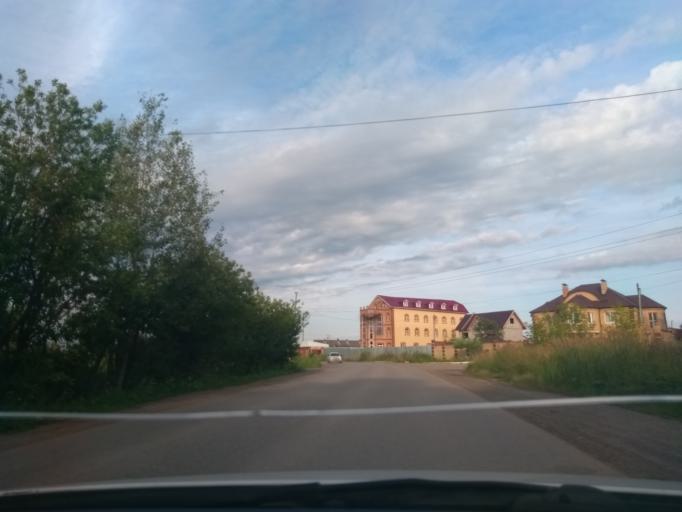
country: RU
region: Perm
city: Perm
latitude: 57.9963
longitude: 56.3336
